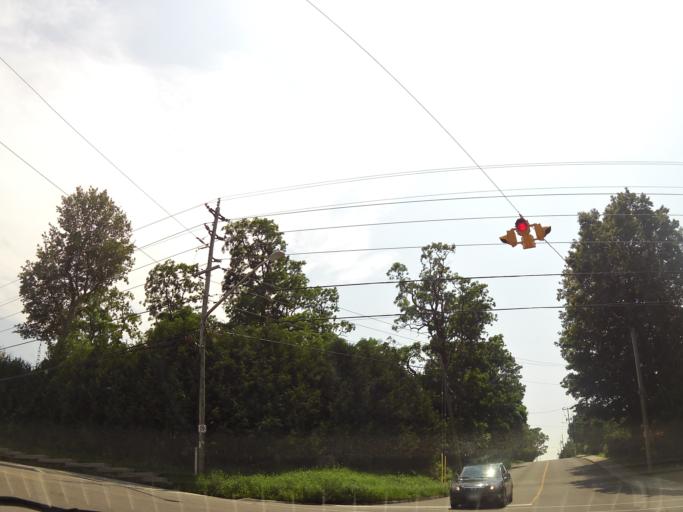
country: CA
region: Ontario
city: Kingston
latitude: 44.4071
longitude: -76.5965
